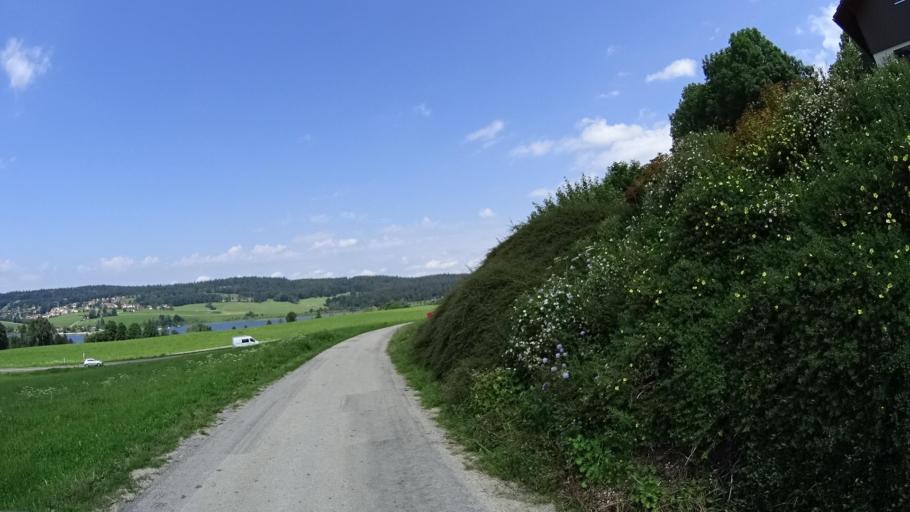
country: FR
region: Franche-Comte
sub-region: Departement du Doubs
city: Les Fourgs
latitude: 46.8219
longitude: 6.3324
